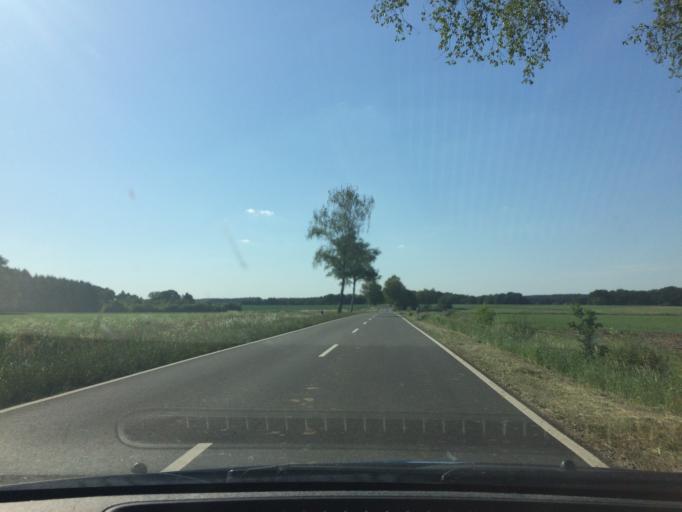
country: DE
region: Lower Saxony
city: Bad Fallingbostel
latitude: 52.9188
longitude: 9.7047
